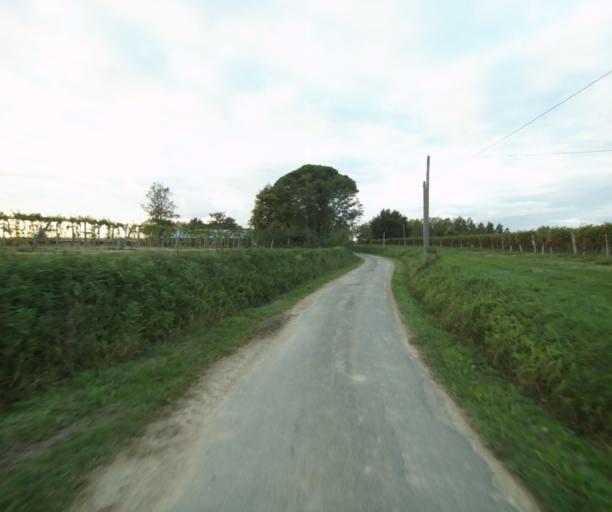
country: FR
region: Aquitaine
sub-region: Departement des Landes
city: Gabarret
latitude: 43.9766
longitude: 0.0883
